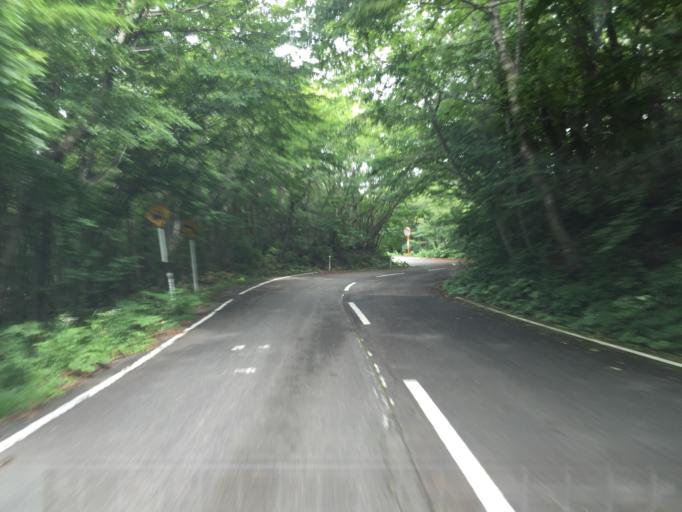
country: JP
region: Fukushima
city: Nihommatsu
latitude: 37.6606
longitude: 140.3241
